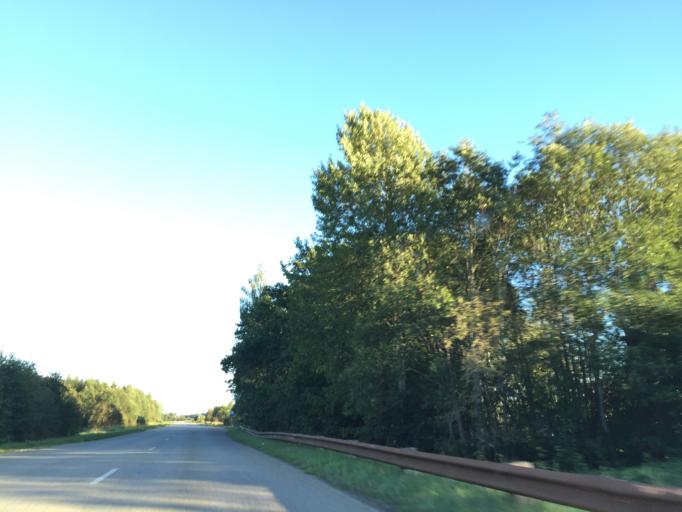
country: LV
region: Kuldigas Rajons
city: Kuldiga
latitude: 56.9418
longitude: 22.0232
